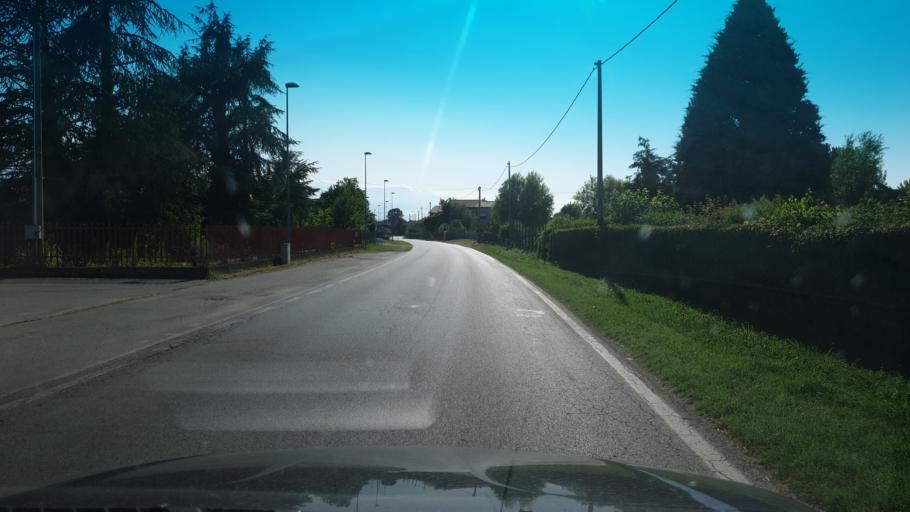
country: IT
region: Veneto
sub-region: Provincia di Rovigo
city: Costa di Rovigo
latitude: 45.0596
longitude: 11.7031
